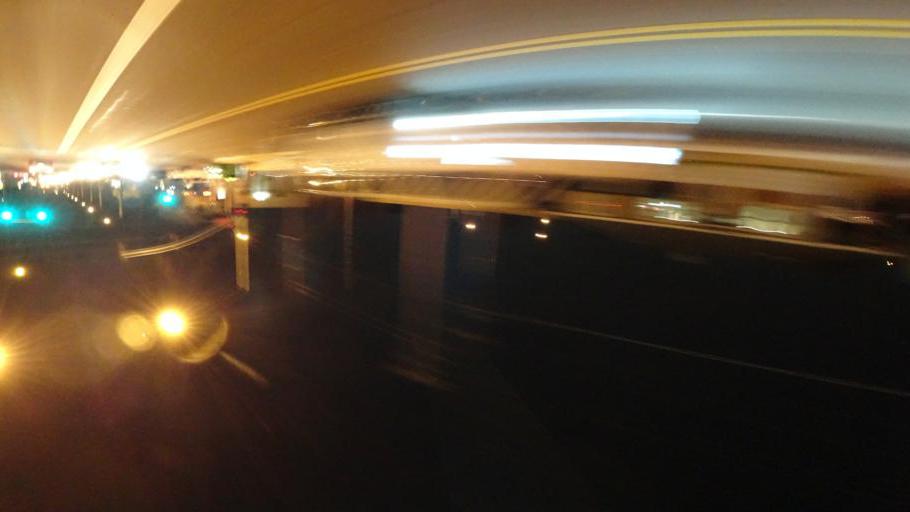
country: US
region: Arizona
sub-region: Maricopa County
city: Mesa
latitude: 33.4223
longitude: -111.8477
